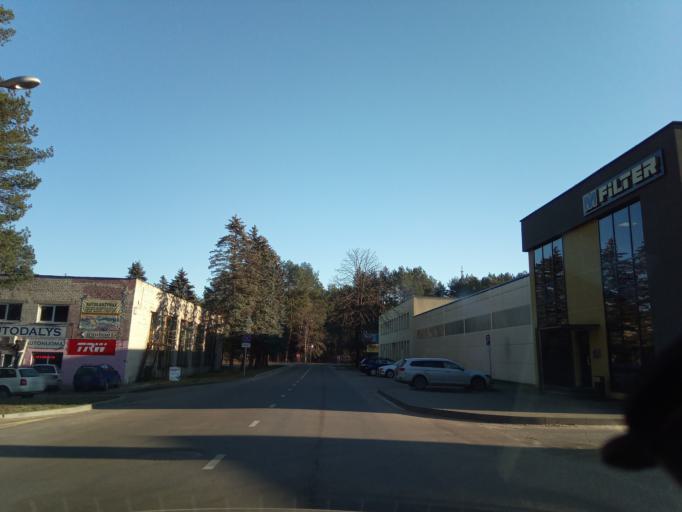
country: LT
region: Alytaus apskritis
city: Druskininkai
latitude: 54.0025
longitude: 23.9799
